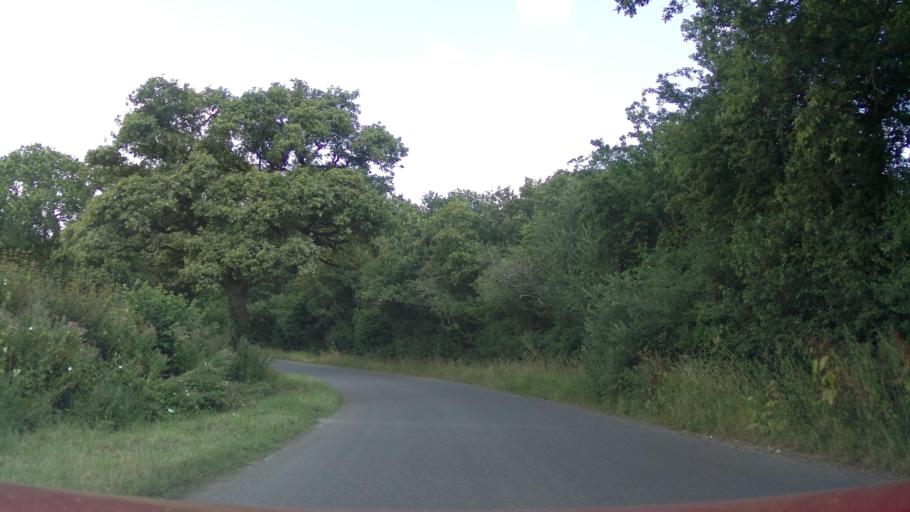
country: GB
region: England
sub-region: Wiltshire
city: Hankerton
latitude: 51.5796
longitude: -2.0096
